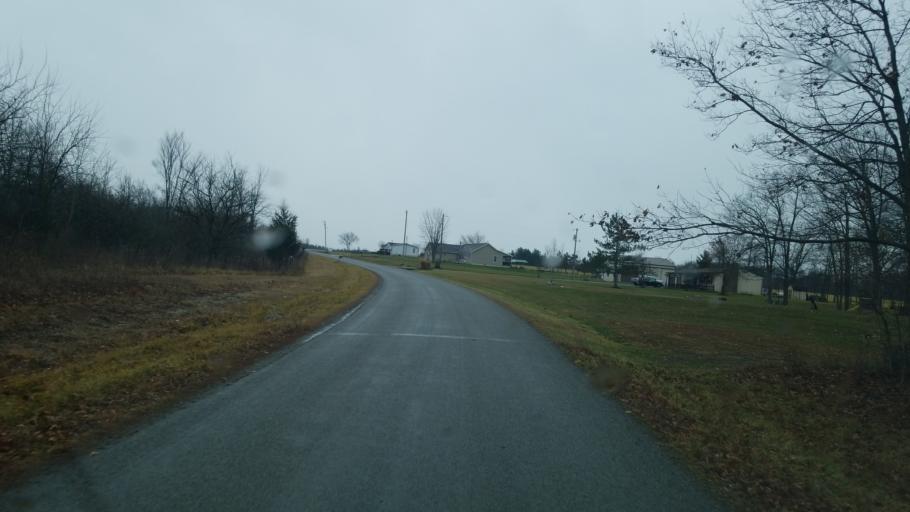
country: US
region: Ohio
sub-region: Logan County
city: Northwood
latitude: 40.4675
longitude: -83.6577
